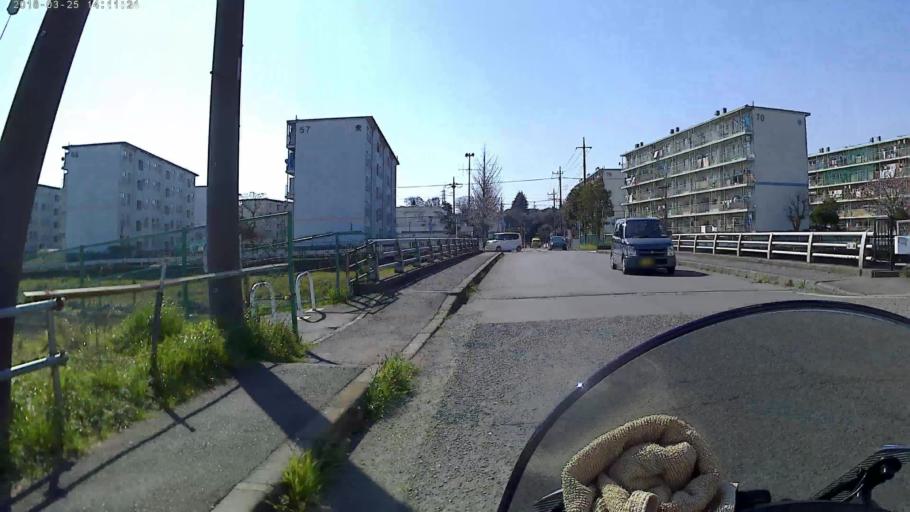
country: JP
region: Kanagawa
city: Minami-rinkan
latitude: 35.4272
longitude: 139.4734
